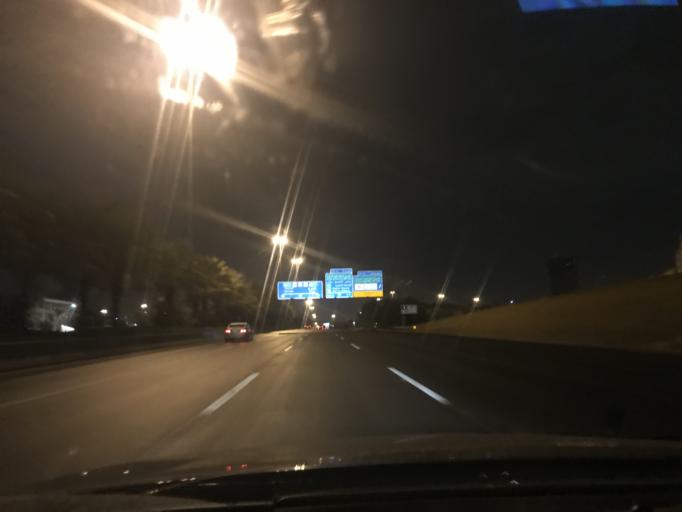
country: SA
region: Ar Riyad
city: Riyadh
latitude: 24.7577
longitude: 46.6399
